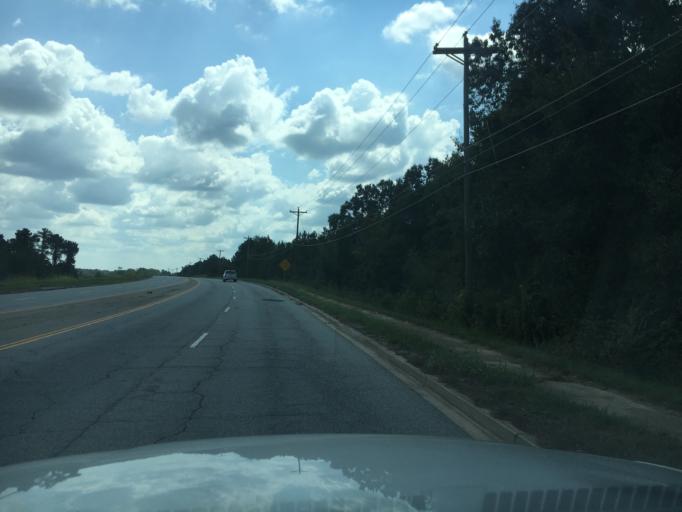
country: US
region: South Carolina
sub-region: Greenwood County
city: Greenwood
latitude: 34.1800
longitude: -82.1841
